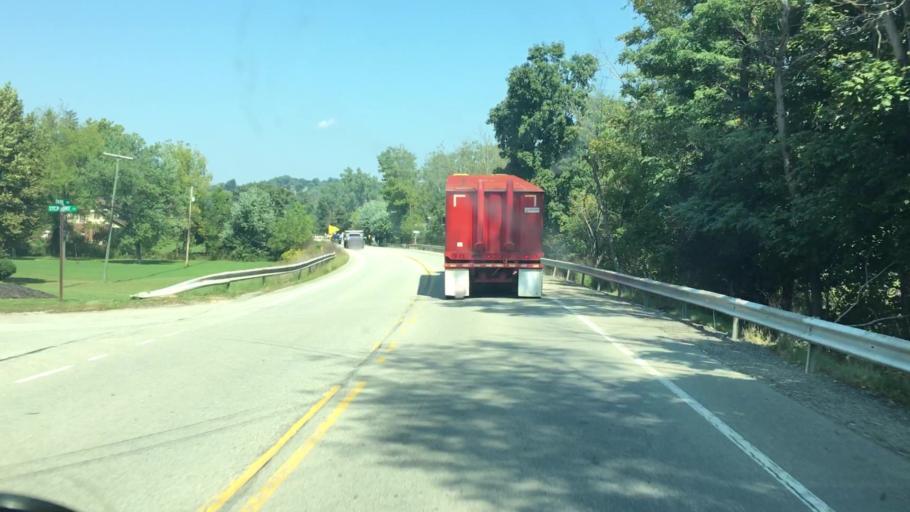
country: US
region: Pennsylvania
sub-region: Washington County
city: Washington
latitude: 40.1414
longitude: -80.2692
